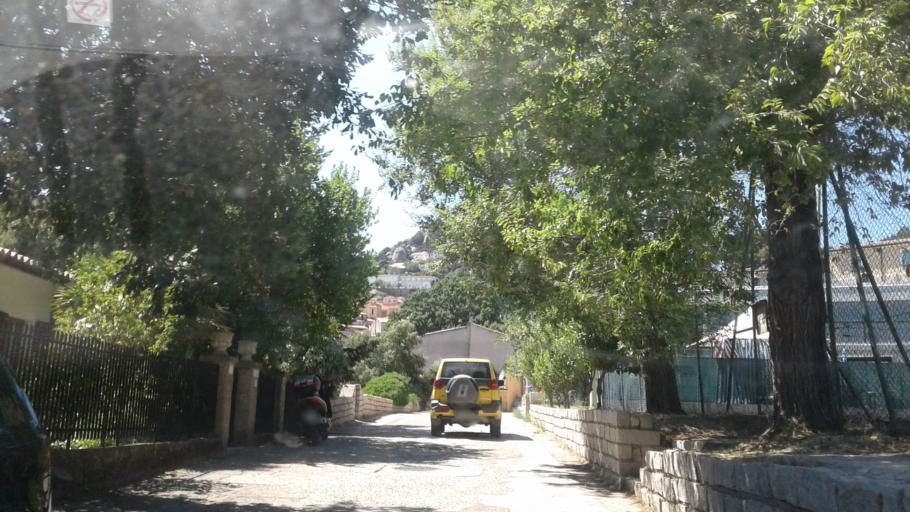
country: IT
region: Sardinia
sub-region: Provincia di Olbia-Tempio
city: Aggius
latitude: 40.9296
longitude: 9.0683
